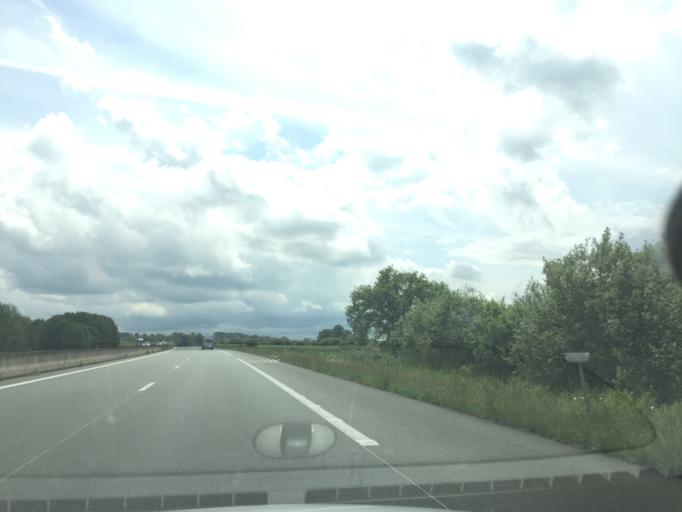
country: FR
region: Pays de la Loire
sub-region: Departement de la Sarthe
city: Ecommoy
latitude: 47.8028
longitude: 0.3035
